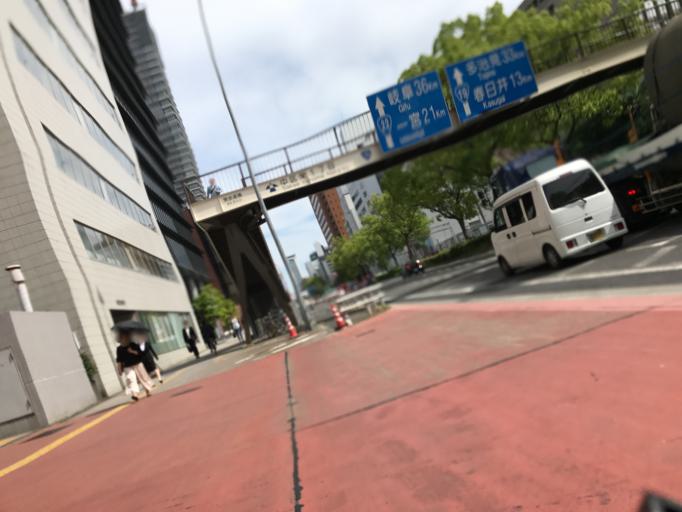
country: JP
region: Aichi
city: Nagoya-shi
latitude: 35.1646
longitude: 136.8977
